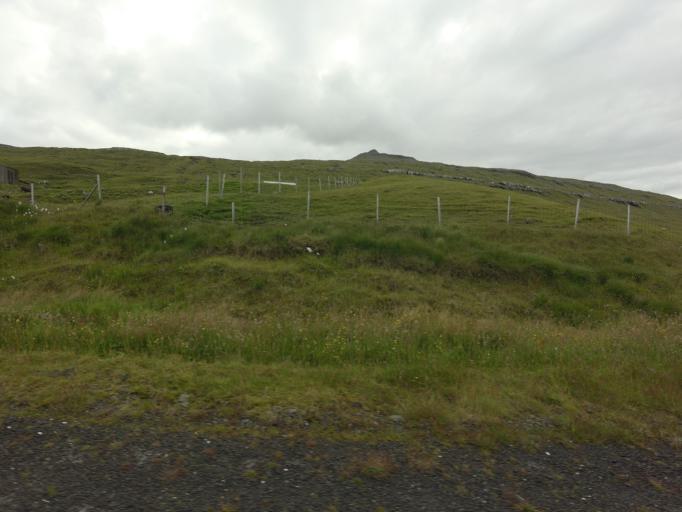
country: FO
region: Eysturoy
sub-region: Eidi
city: Eidi
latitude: 62.2119
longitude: -6.9975
